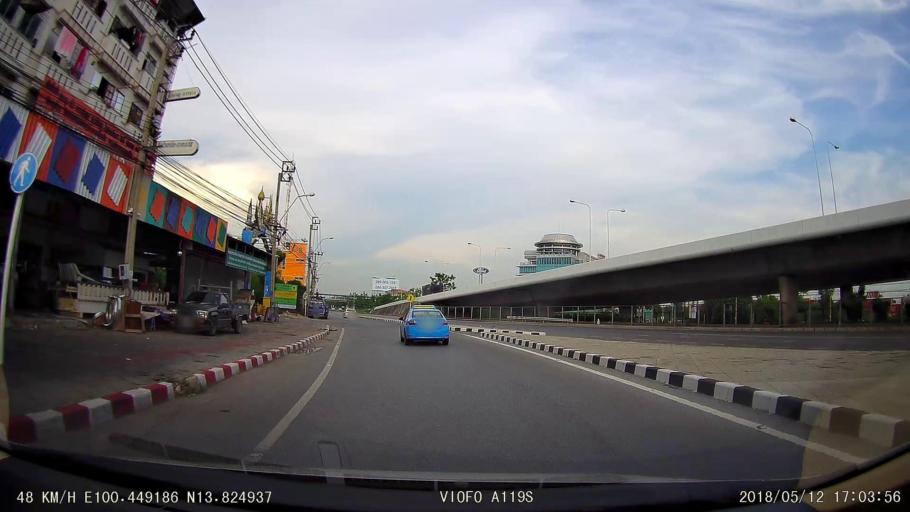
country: TH
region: Nonthaburi
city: Bang Kruai
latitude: 13.8249
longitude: 100.4493
